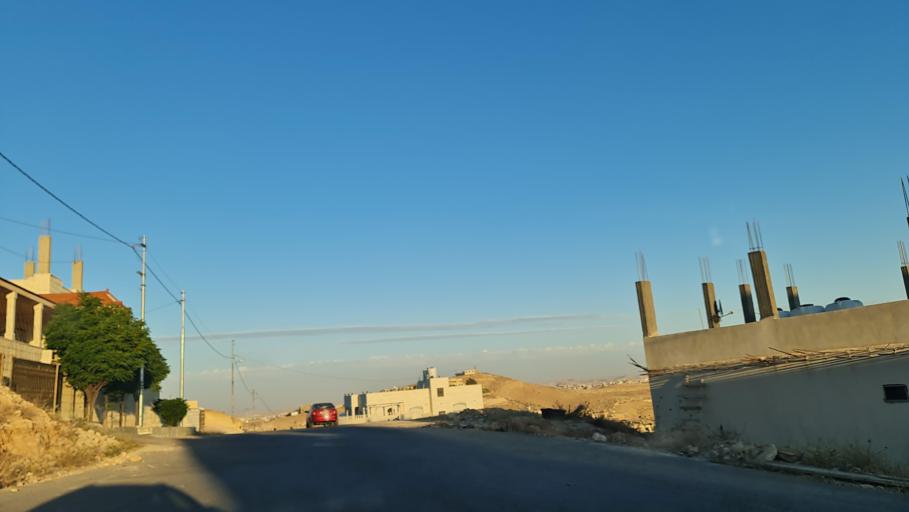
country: JO
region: Zarqa
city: Zarqa
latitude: 32.0893
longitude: 36.0191
